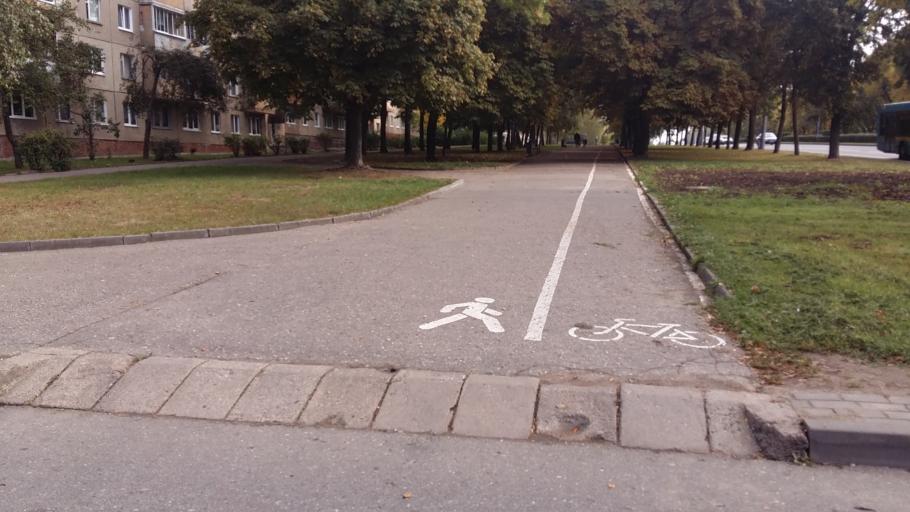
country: BY
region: Grodnenskaya
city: Hrodna
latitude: 53.6976
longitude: 23.8043
